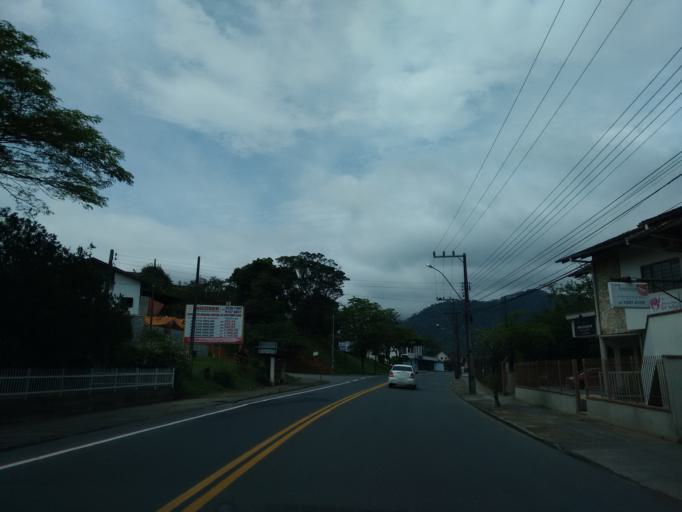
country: BR
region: Santa Catarina
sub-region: Pomerode
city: Pomerode
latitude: -26.7223
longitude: -49.1684
